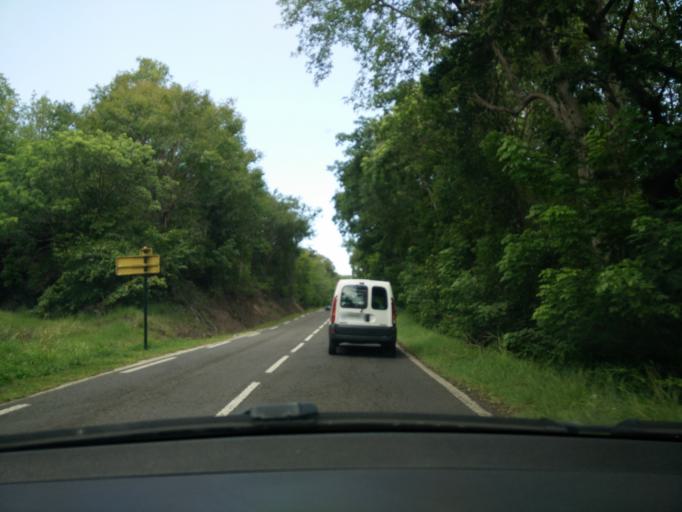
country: GP
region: Guadeloupe
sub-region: Guadeloupe
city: Sainte-Rose
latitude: 16.3528
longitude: -61.7632
